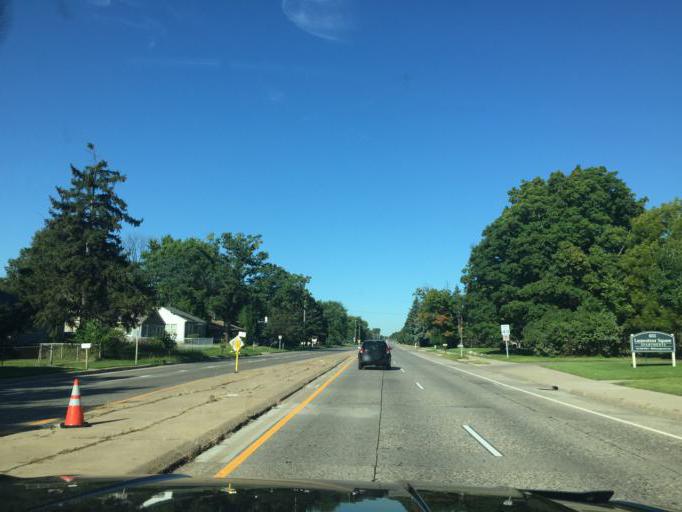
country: US
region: Minnesota
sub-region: Ramsey County
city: Roseville
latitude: 44.9918
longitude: -93.1273
